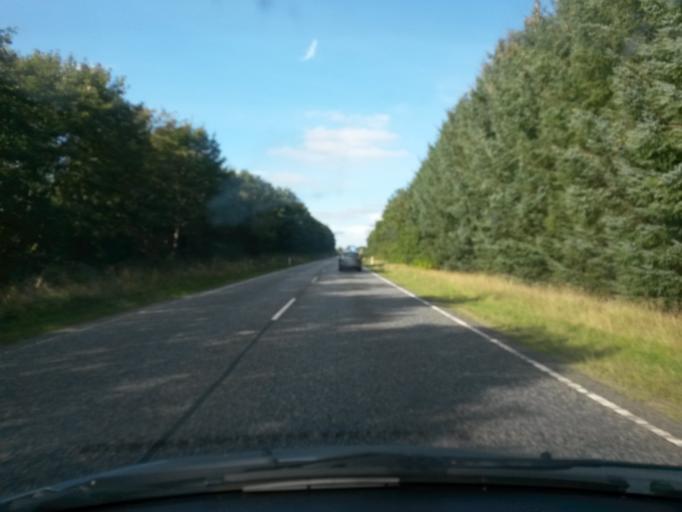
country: DK
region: Central Jutland
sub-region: Herning Kommune
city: Avlum
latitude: 56.2400
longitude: 8.8045
